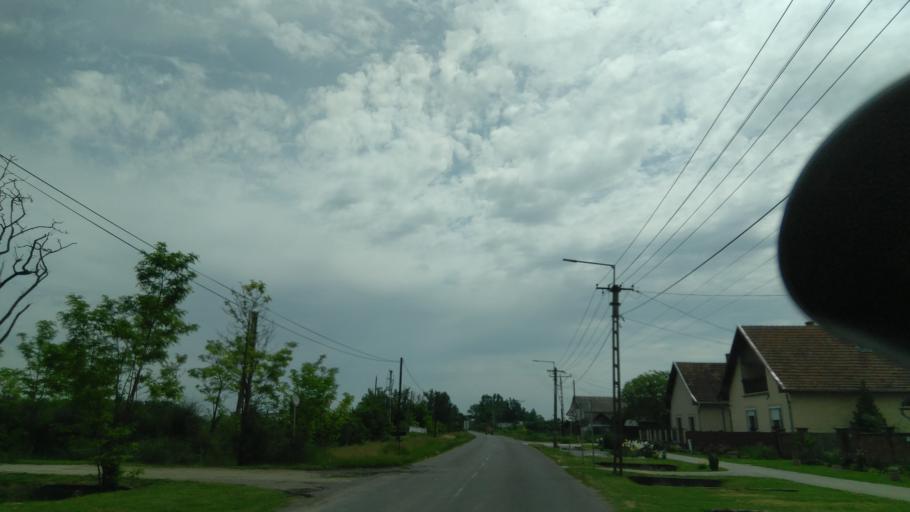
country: HU
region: Bekes
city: Fuzesgyarmat
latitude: 47.1003
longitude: 21.2231
